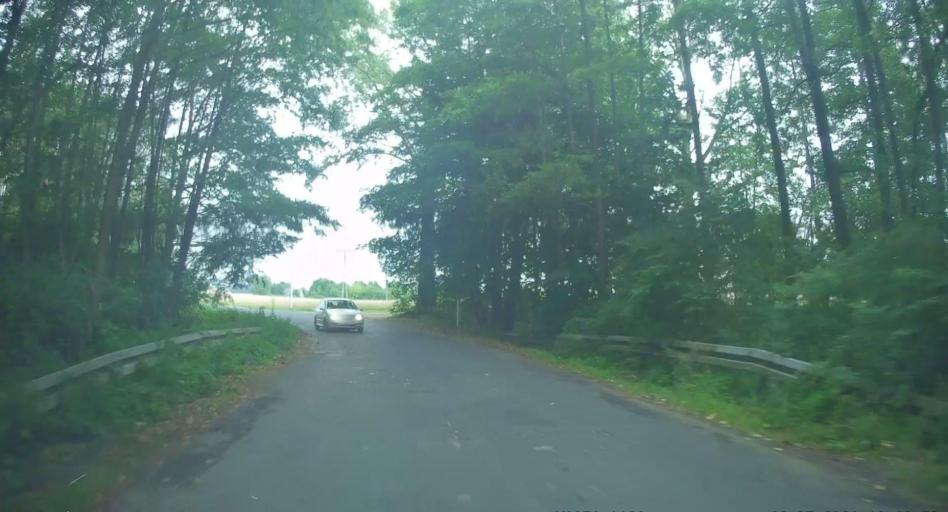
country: PL
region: Lodz Voivodeship
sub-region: Powiat rawski
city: Rawa Mazowiecka
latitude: 51.7395
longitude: 20.1904
